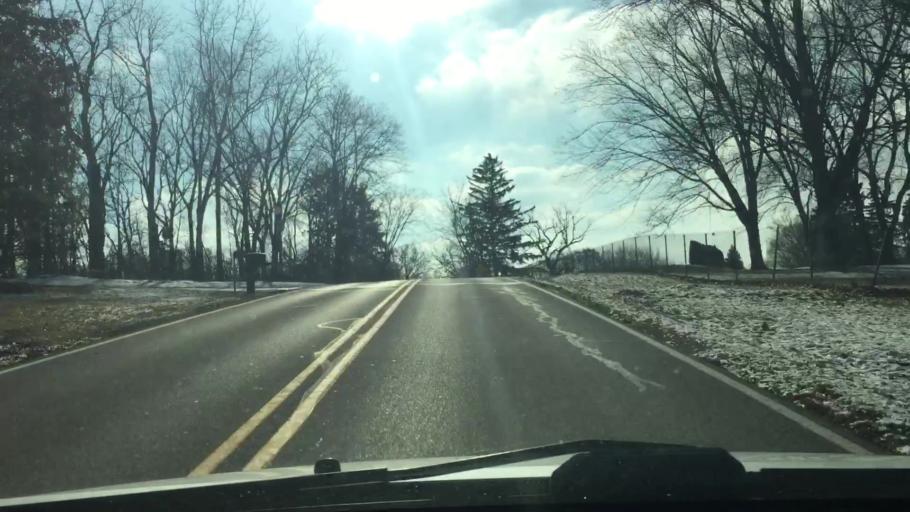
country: US
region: Wisconsin
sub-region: Waukesha County
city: Waukesha
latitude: 42.9857
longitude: -88.2871
